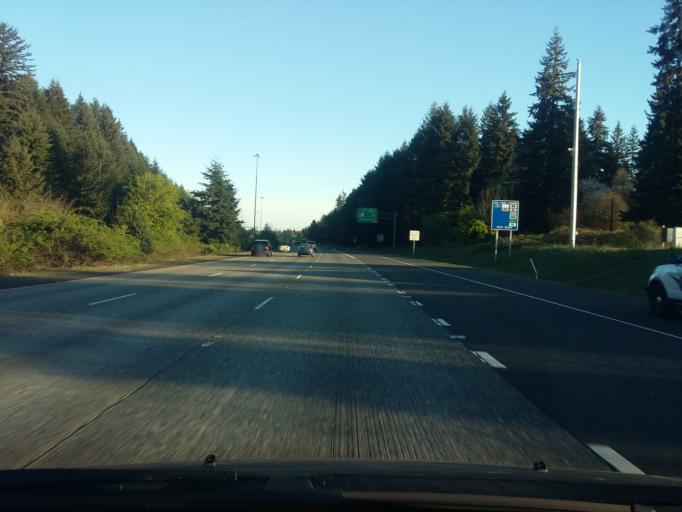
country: US
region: Washington
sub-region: Clark County
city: Orchards
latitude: 45.6649
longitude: -122.5782
